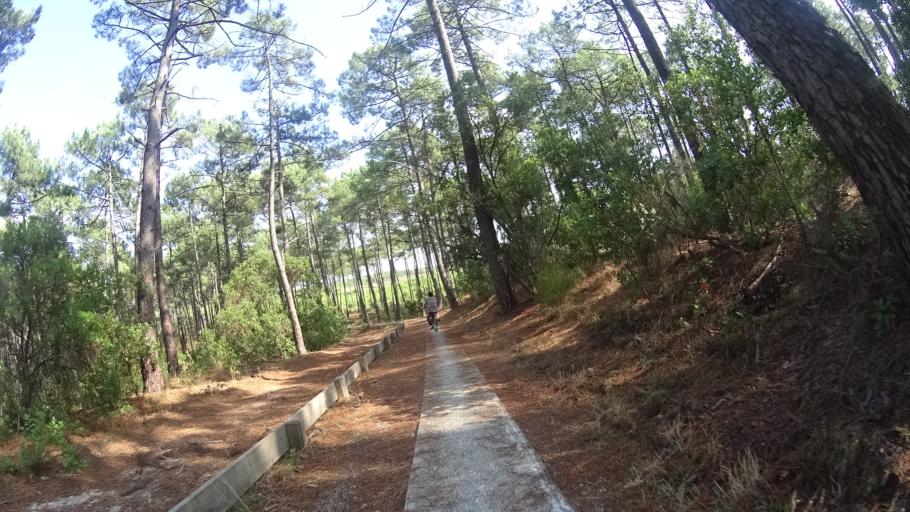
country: FR
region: Aquitaine
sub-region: Departement de la Gironde
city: Lacanau
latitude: 44.9632
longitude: -1.1948
